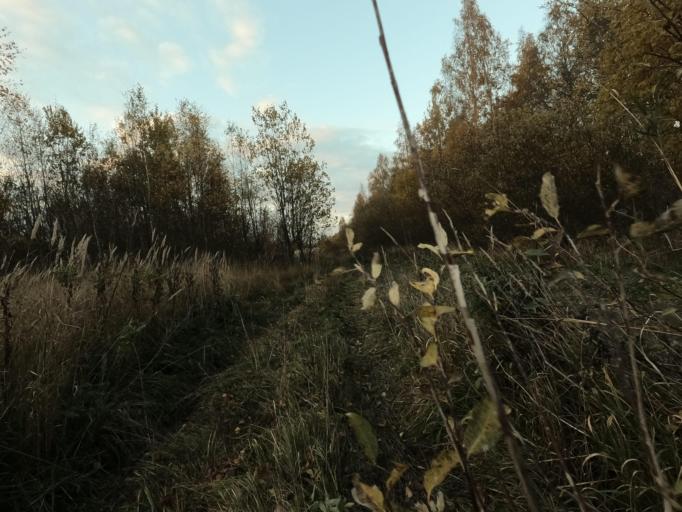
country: RU
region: Leningrad
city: Mga
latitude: 59.8158
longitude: 31.1777
